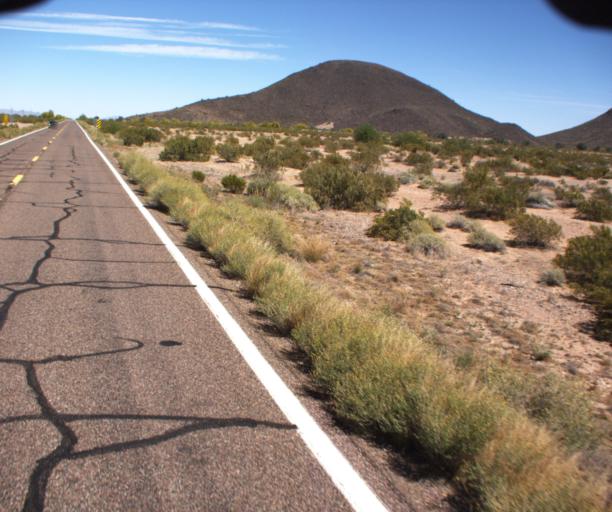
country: US
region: Arizona
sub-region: Maricopa County
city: Gila Bend
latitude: 32.7406
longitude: -112.8308
